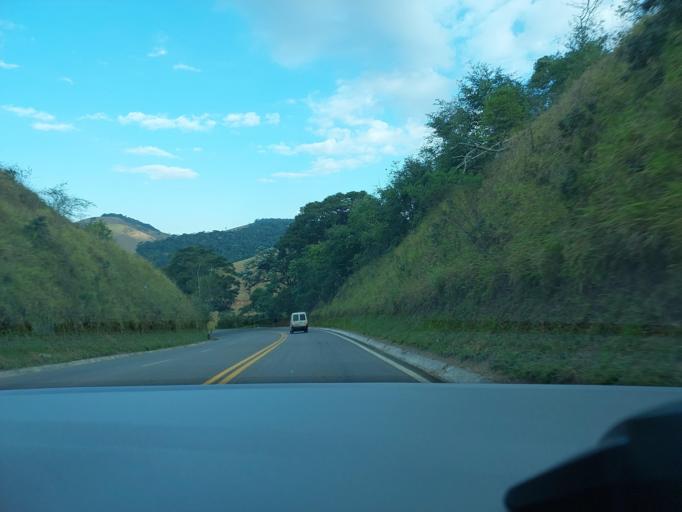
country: BR
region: Minas Gerais
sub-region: Mirai
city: Mirai
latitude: -21.0479
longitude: -42.5235
